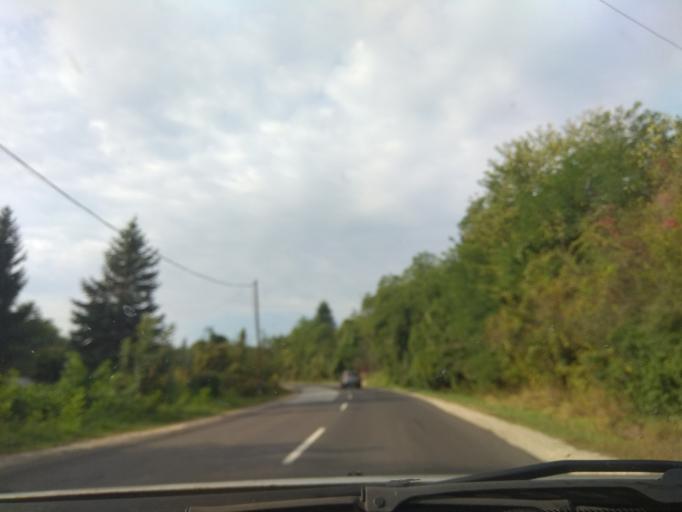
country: HU
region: Borsod-Abauj-Zemplen
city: Miskolc
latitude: 48.0886
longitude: 20.7528
